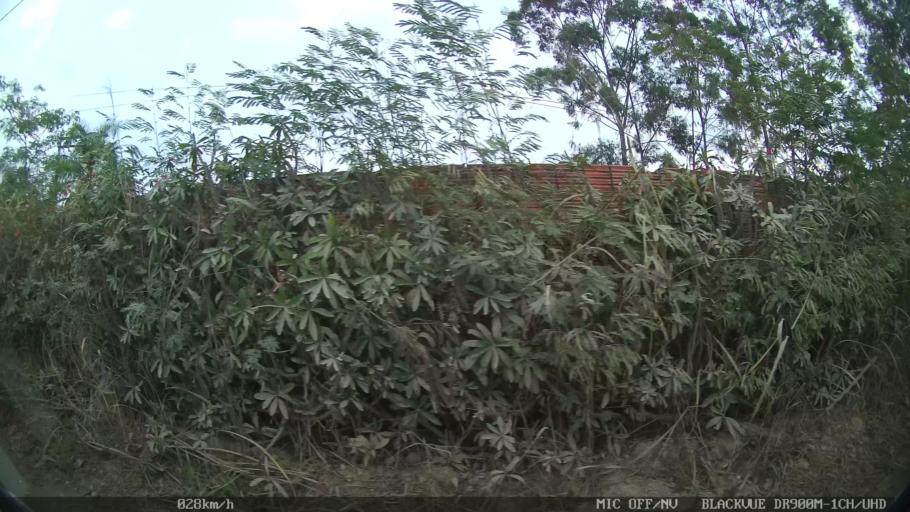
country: BR
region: Sao Paulo
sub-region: Americana
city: Americana
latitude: -22.6639
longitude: -47.3745
